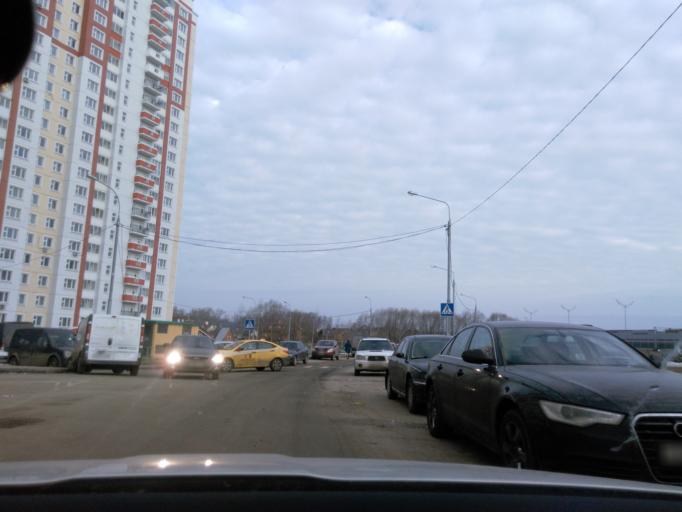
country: RU
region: Moskovskaya
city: Levoberezhnaya
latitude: 55.9034
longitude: 37.4791
